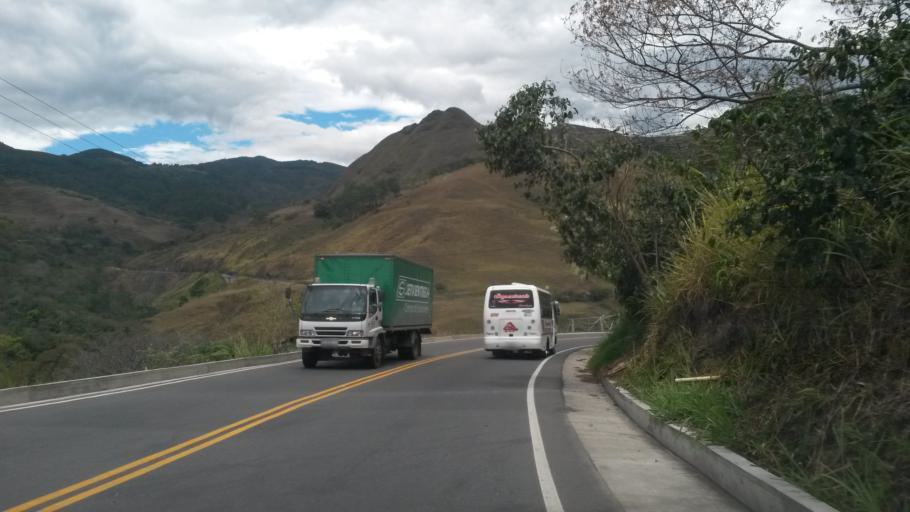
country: CO
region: Cauca
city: Rosas
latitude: 2.2806
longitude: -76.7126
